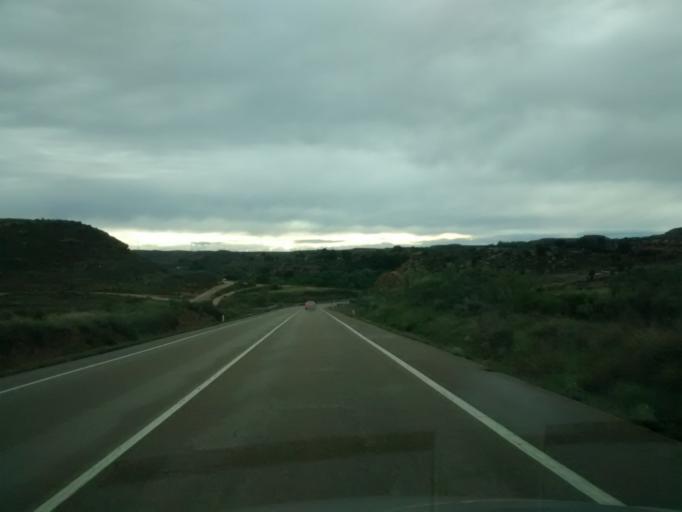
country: ES
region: Aragon
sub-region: Provincia de Zaragoza
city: Caspe
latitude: 41.2080
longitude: 0.0167
